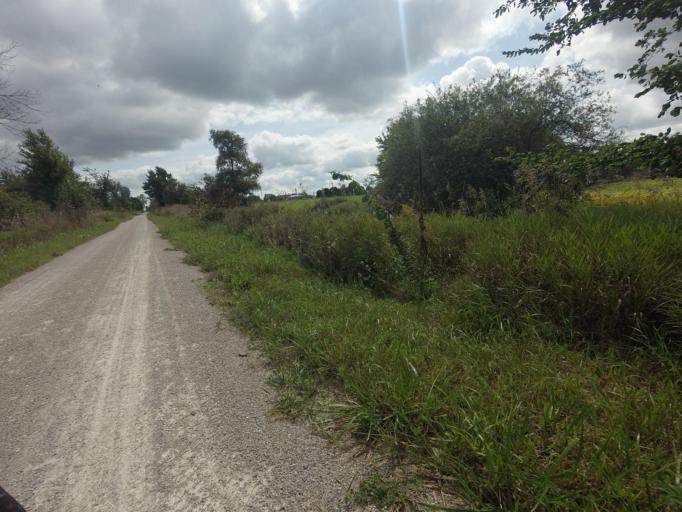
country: CA
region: Ontario
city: North Perth
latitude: 43.5778
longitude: -81.0520
